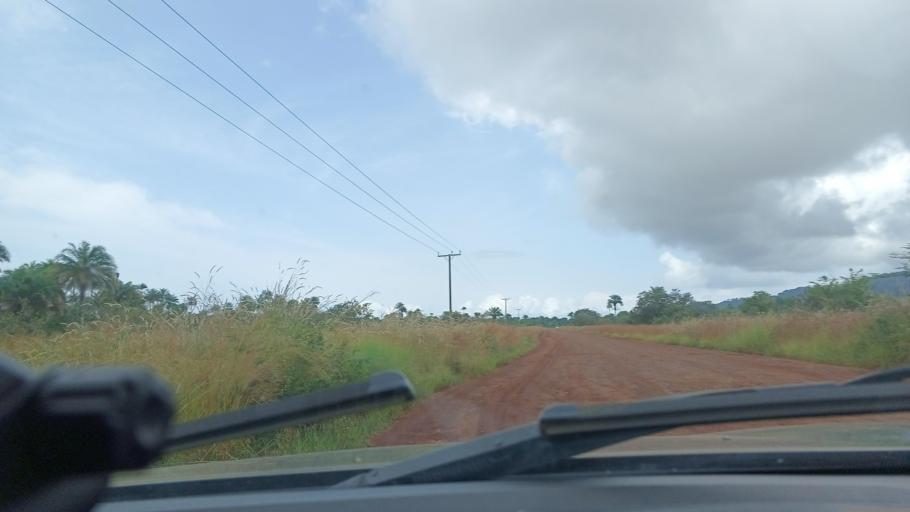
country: LR
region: Grand Cape Mount
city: Robertsport
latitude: 6.7031
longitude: -11.3141
